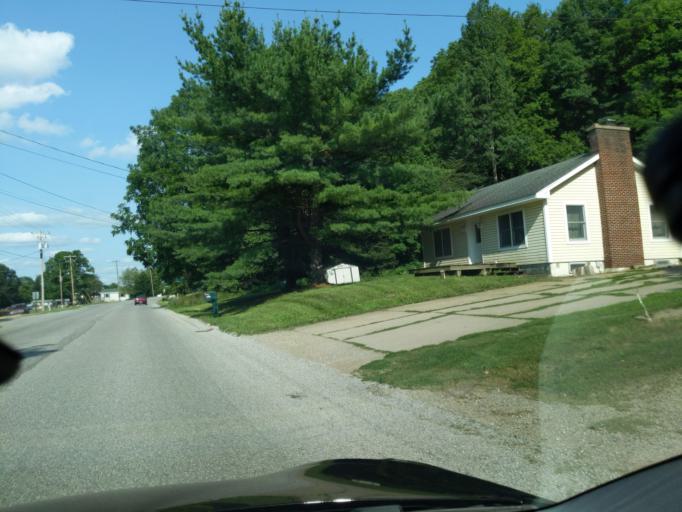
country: US
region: Michigan
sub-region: Kent County
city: Lowell
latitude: 42.9257
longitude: -85.3329
